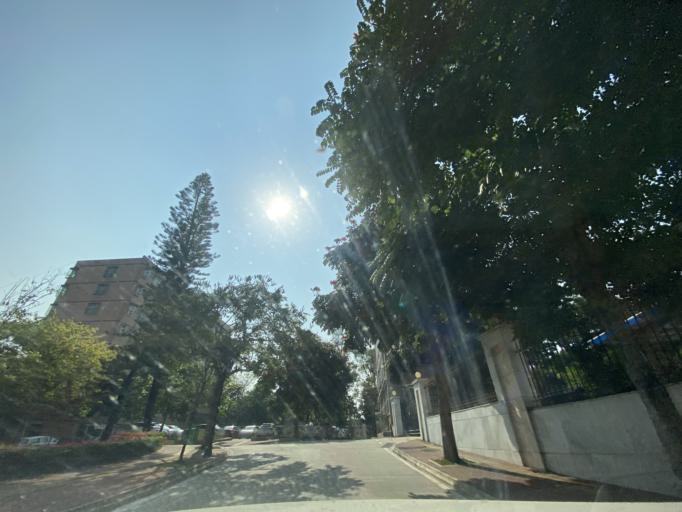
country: CN
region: Hainan
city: Chongshan
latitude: 18.7760
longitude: 109.5133
